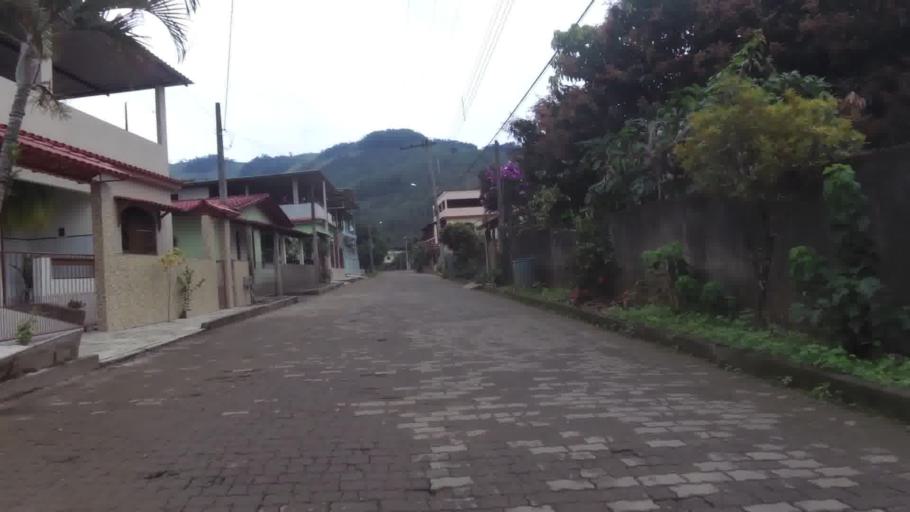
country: BR
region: Espirito Santo
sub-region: Iconha
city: Iconha
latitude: -20.7667
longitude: -40.8350
